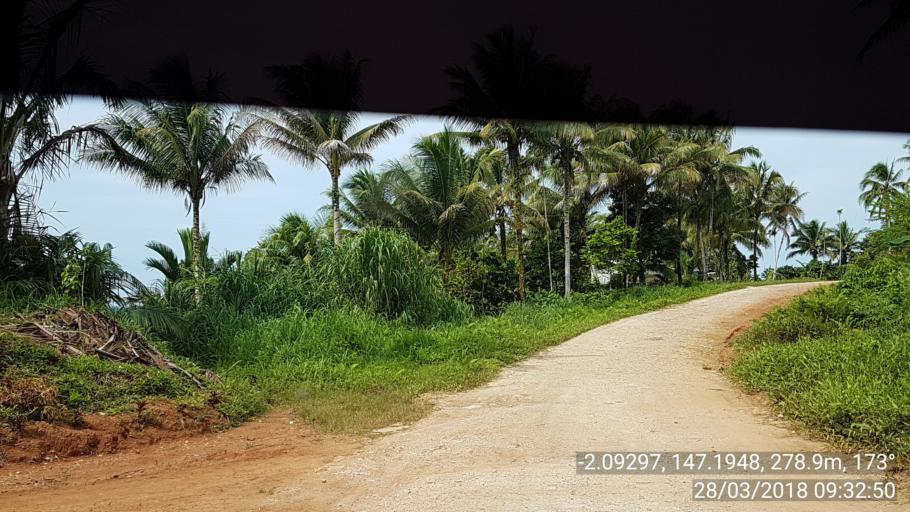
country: PG
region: Manus
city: Lorengau
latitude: -2.0930
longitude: 147.1949
